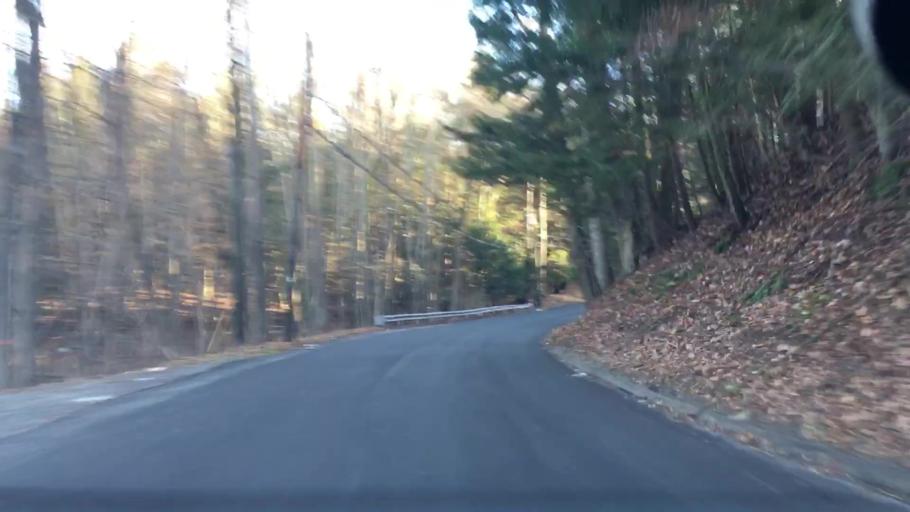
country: US
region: Connecticut
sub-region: Fairfield County
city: Newtown
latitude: 41.4585
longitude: -73.3259
